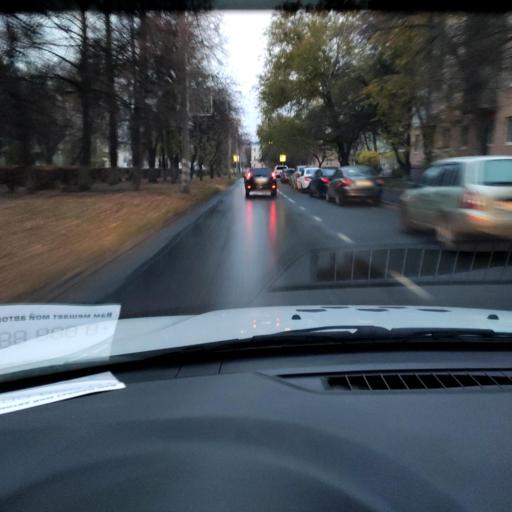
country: RU
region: Samara
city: Tol'yatti
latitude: 53.5090
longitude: 49.4118
